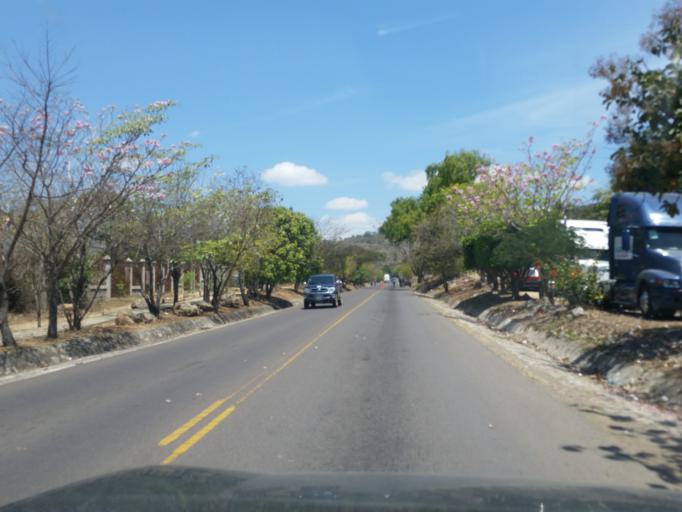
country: NI
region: Esteli
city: Esteli
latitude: 13.0199
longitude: -86.3127
